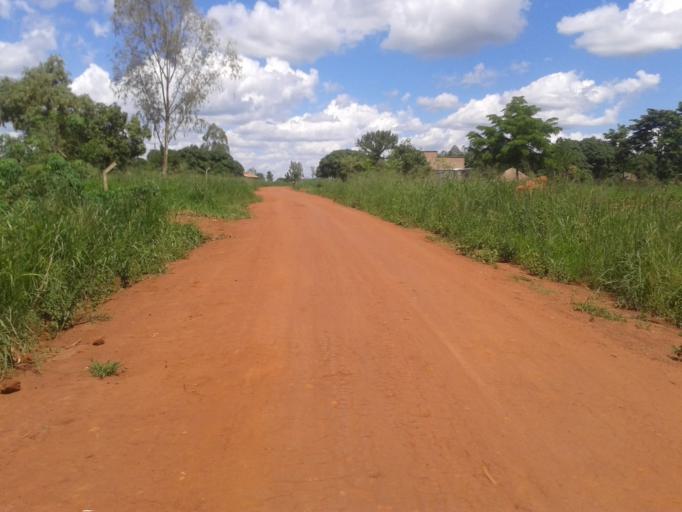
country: UG
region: Northern Region
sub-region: Gulu District
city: Gulu
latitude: 2.7595
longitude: 32.3237
